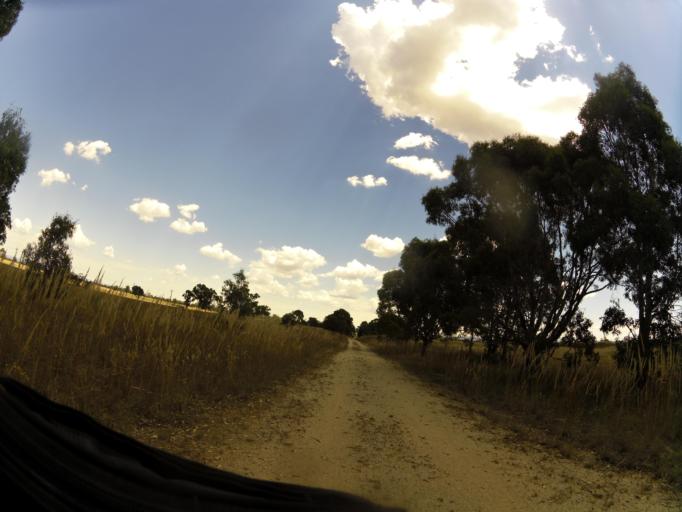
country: AU
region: Victoria
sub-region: Wellington
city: Heyfield
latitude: -37.9827
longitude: 146.8297
